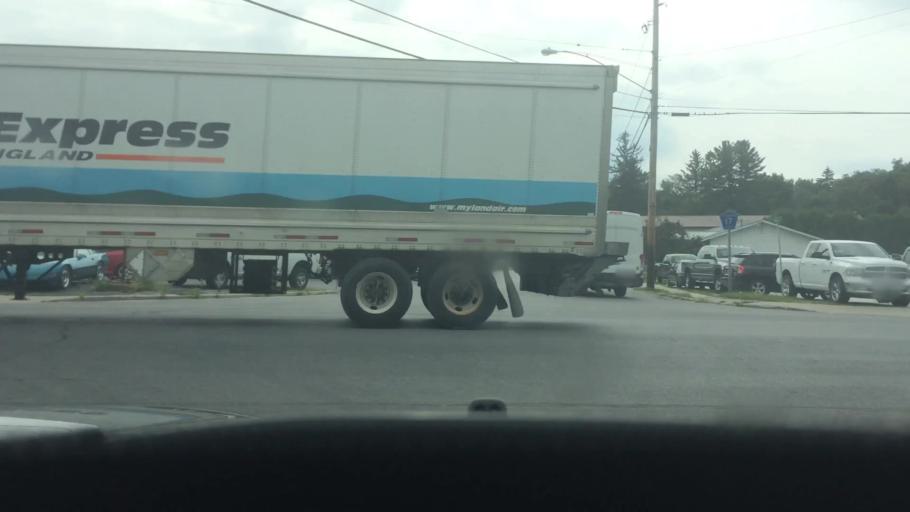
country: US
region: New York
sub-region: St. Lawrence County
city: Canton
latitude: 44.5052
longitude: -75.2738
